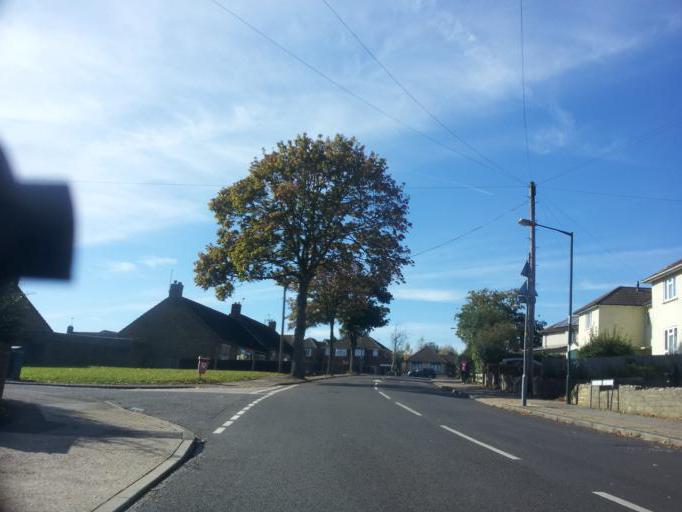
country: GB
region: England
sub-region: Kent
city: Chatham
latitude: 51.3533
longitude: 0.5240
